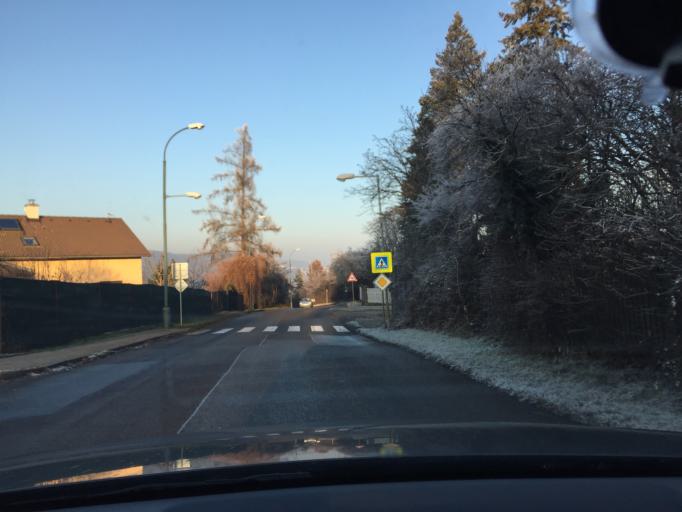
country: CZ
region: Central Bohemia
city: Cernosice
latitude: 49.9539
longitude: 14.3198
